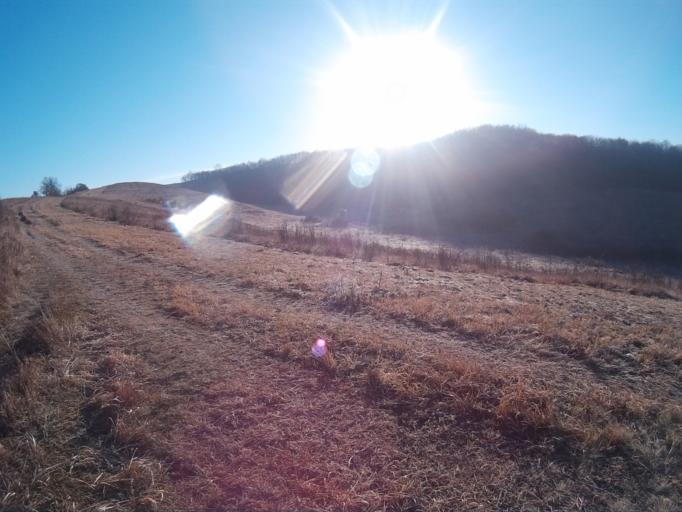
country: HU
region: Borsod-Abauj-Zemplen
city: Putnok
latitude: 48.3768
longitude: 20.4399
